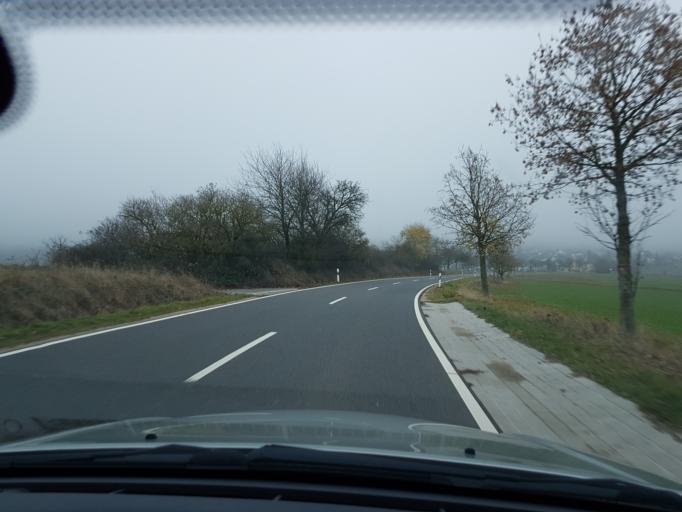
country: DE
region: Hesse
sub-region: Regierungsbezirk Darmstadt
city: Bad Schwalbach
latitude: 50.0898
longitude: 8.0409
